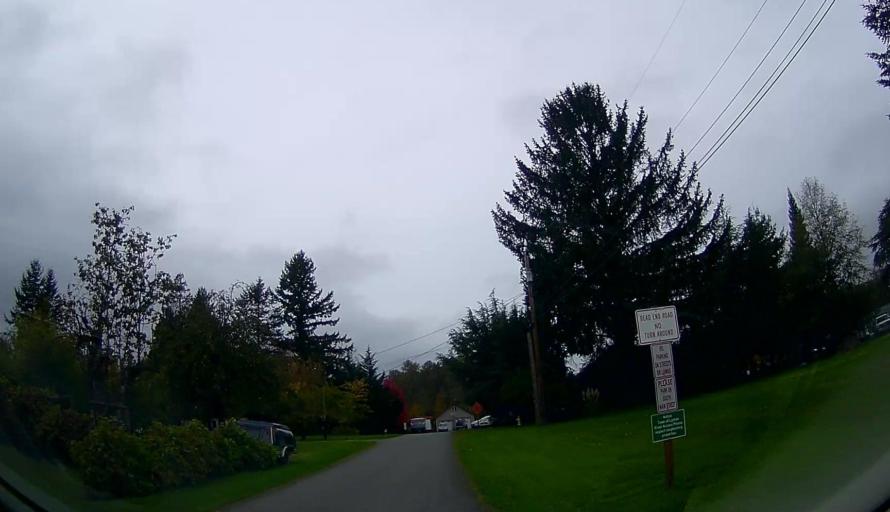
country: US
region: Washington
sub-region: Skagit County
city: Sedro-Woolley
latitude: 48.5240
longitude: -122.0601
